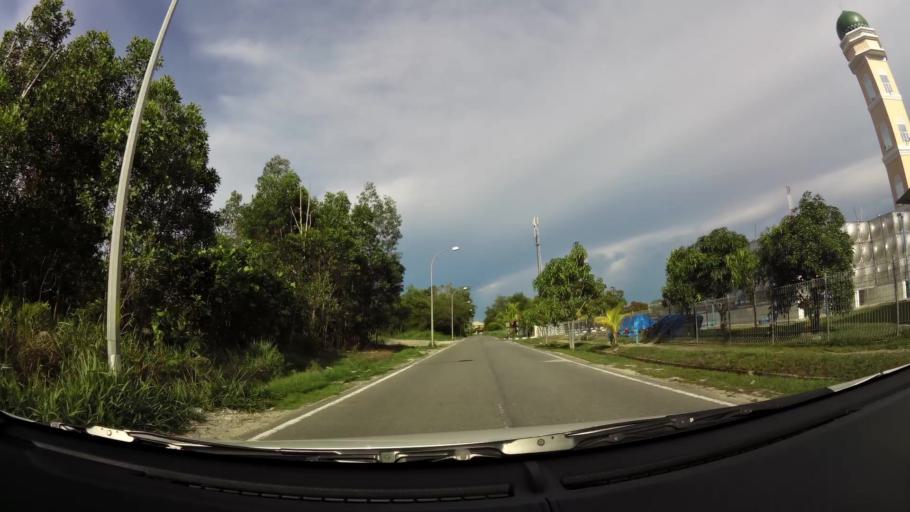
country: BN
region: Brunei and Muara
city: Bandar Seri Begawan
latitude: 4.9677
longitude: 115.0300
